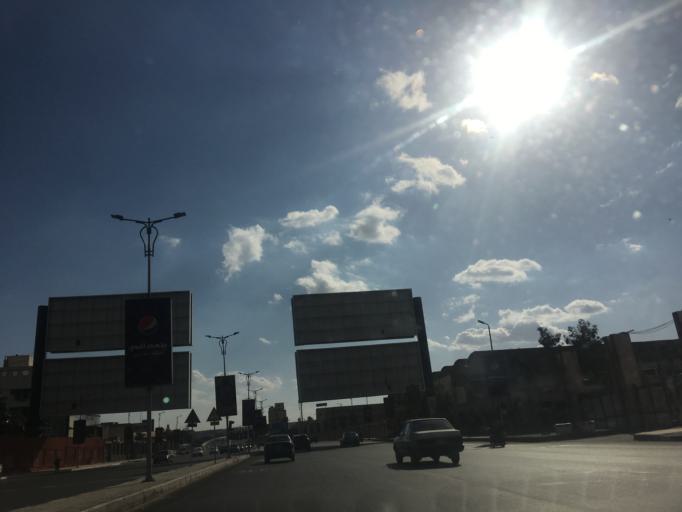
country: EG
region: Muhafazat al Qahirah
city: Cairo
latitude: 30.0491
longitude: 31.3074
